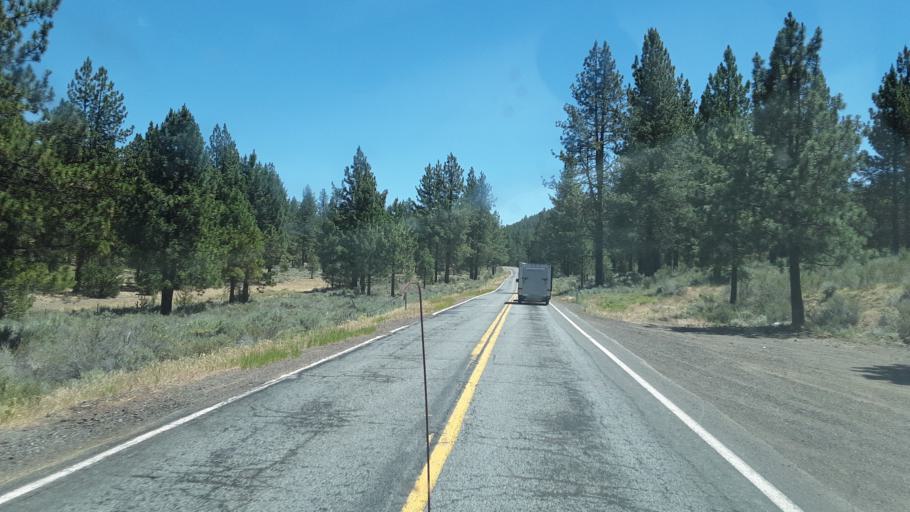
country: US
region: California
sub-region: Modoc County
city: Alturas
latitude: 40.9837
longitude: -120.7949
